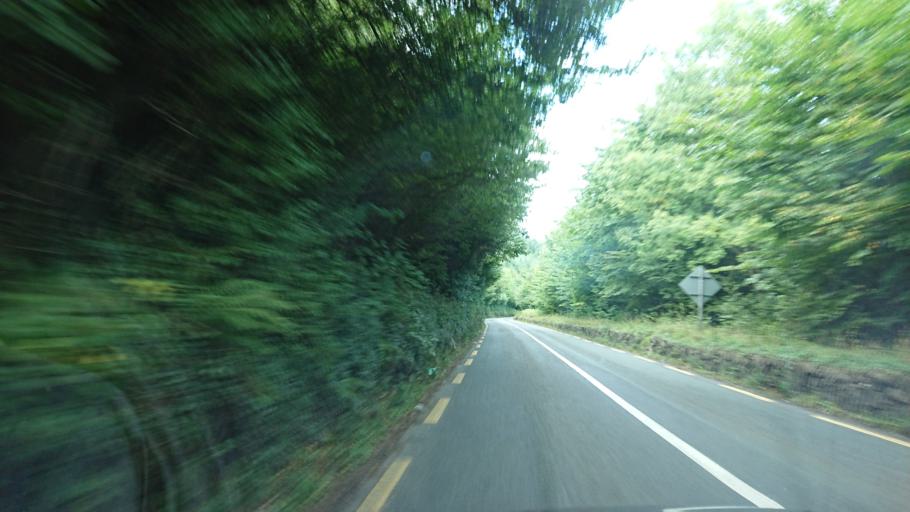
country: IE
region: Munster
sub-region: Waterford
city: Dungarvan
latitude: 52.1195
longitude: -7.6878
